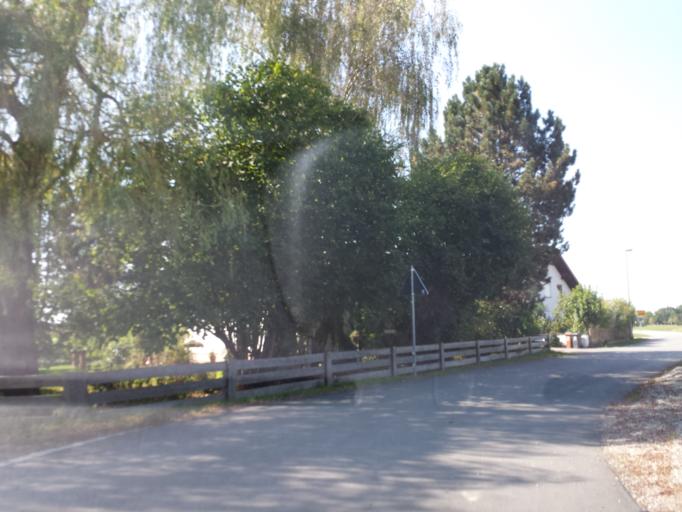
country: DE
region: Bavaria
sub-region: Swabia
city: Tussenhausen
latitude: 48.0698
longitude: 10.5786
